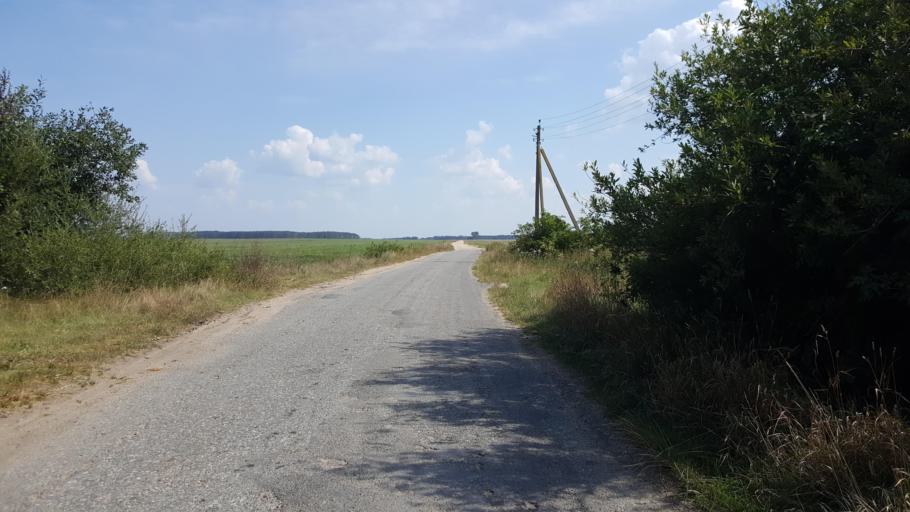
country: BY
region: Brest
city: Kamyanyuki
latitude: 52.4917
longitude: 23.5869
